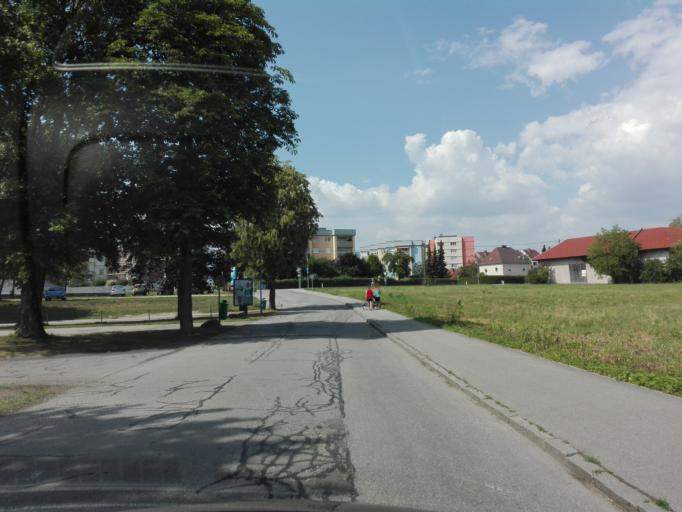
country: AT
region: Upper Austria
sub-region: Politischer Bezirk Linz-Land
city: Traun
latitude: 48.2163
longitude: 14.2237
